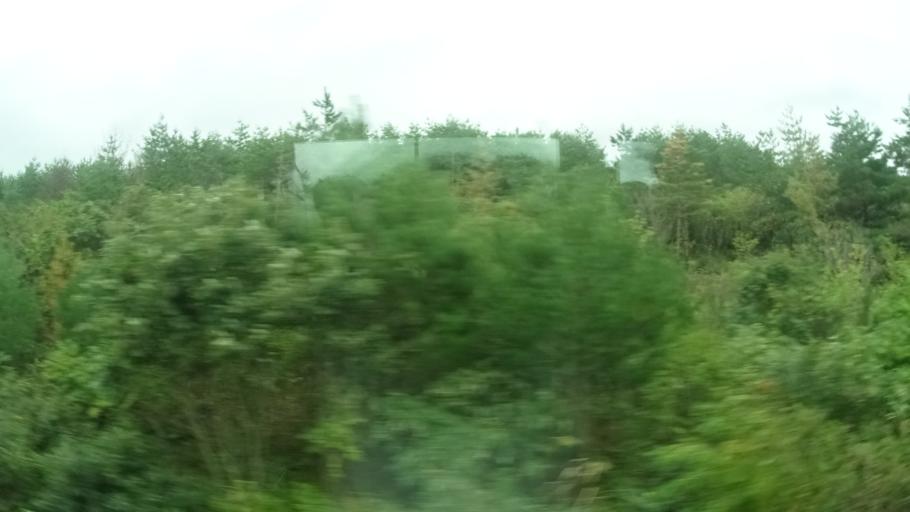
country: JP
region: Niigata
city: Murakami
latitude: 38.2980
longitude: 139.4505
